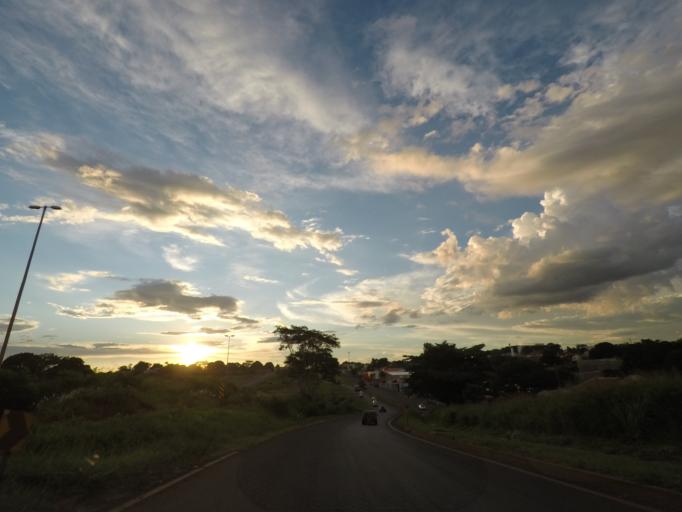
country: BR
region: Minas Gerais
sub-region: Uberaba
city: Uberaba
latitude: -19.7783
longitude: -47.9323
